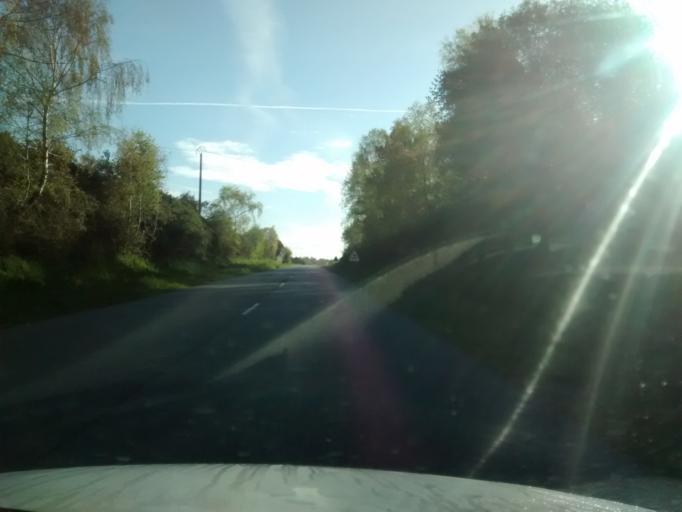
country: FR
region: Brittany
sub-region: Departement du Morbihan
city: Ruffiac
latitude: 47.8093
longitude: -2.3129
